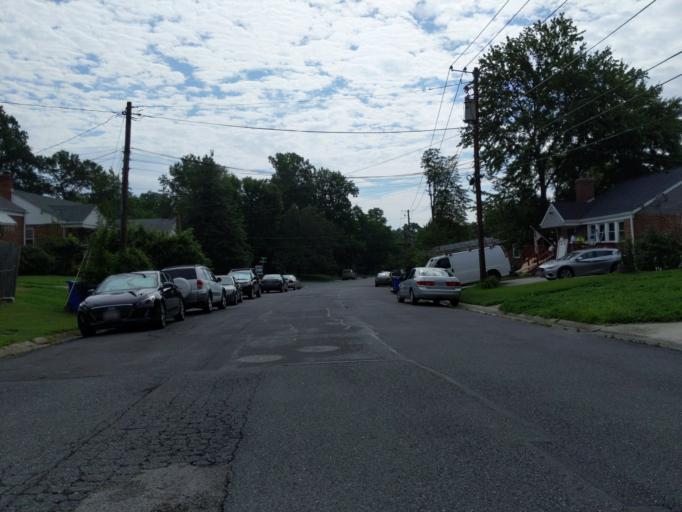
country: US
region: Maryland
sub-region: Montgomery County
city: Kemp Mill
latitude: 39.0320
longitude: -77.0339
